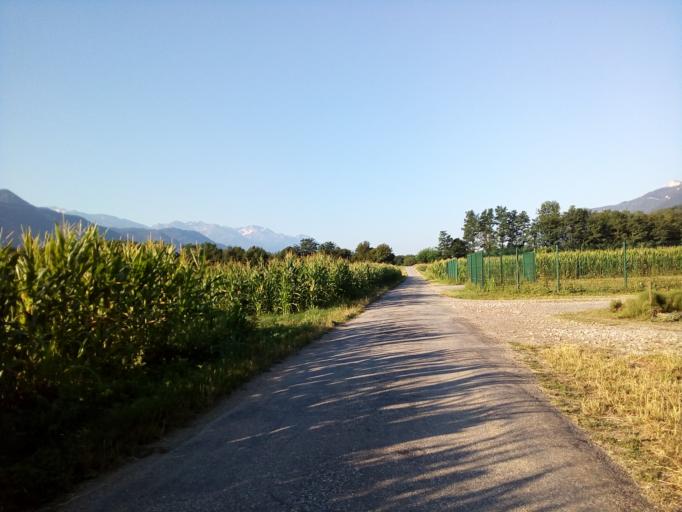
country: FR
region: Rhone-Alpes
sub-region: Departement de l'Isere
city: Barraux
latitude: 45.4044
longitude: 5.9852
